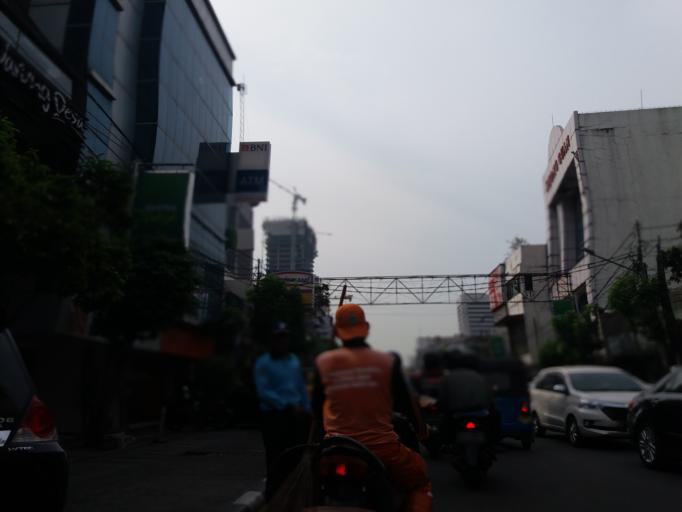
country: ID
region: Jakarta Raya
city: Jakarta
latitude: -6.1864
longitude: 106.8251
